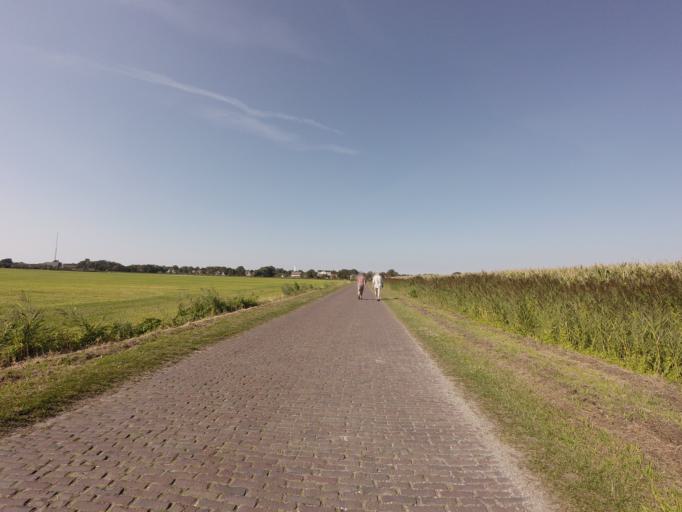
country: NL
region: Friesland
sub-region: Gemeente Schiermonnikoog
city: Schiermonnikoog
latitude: 53.4727
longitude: 6.1615
